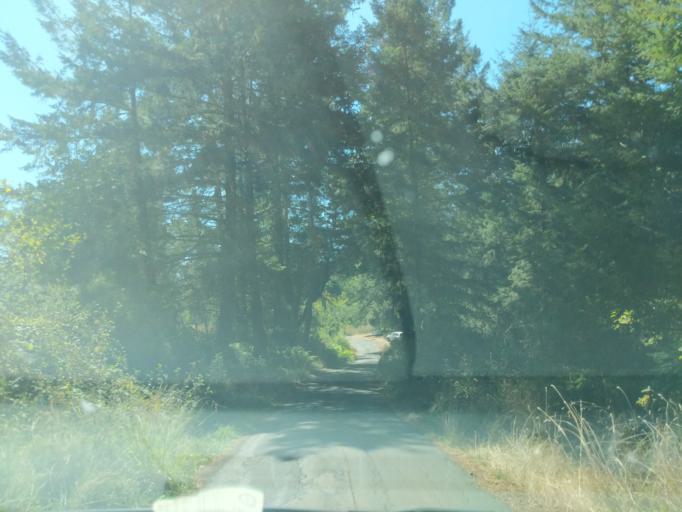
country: US
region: California
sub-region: Sonoma County
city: Monte Rio
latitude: 38.5243
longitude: -123.2401
